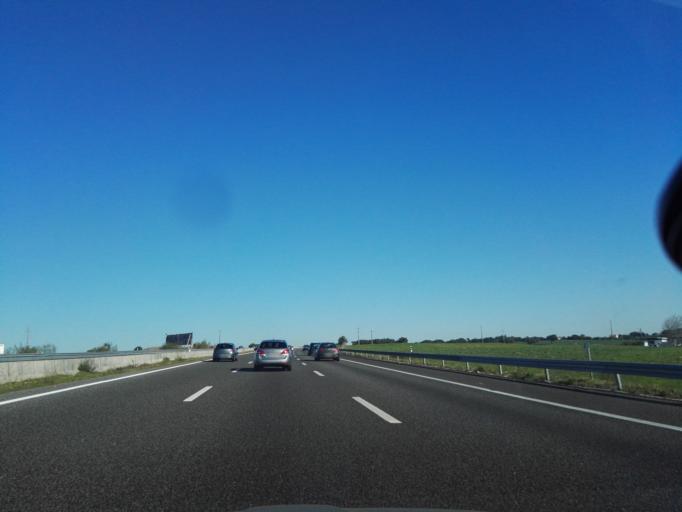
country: PT
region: Santarem
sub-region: Cartaxo
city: Pontevel
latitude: 39.1692
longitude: -8.8499
